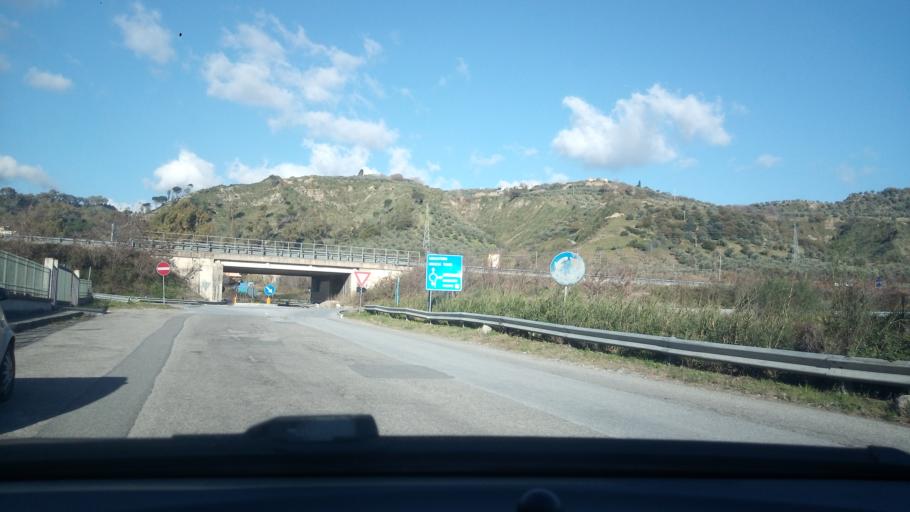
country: IT
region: Calabria
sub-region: Provincia di Catanzaro
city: Settingiano
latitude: 38.8961
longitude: 16.5352
